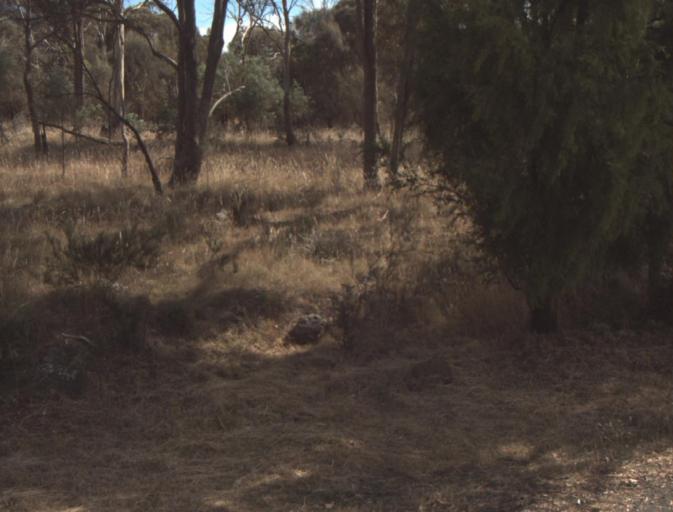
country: AU
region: Tasmania
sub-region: Launceston
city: Summerhill
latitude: -41.4727
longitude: 147.1163
